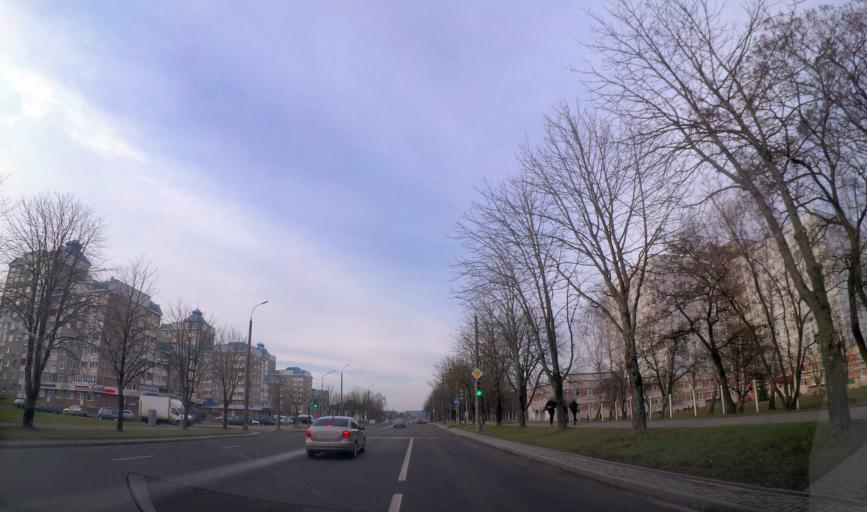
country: BY
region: Grodnenskaya
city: Hrodna
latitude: 53.6726
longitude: 23.7984
